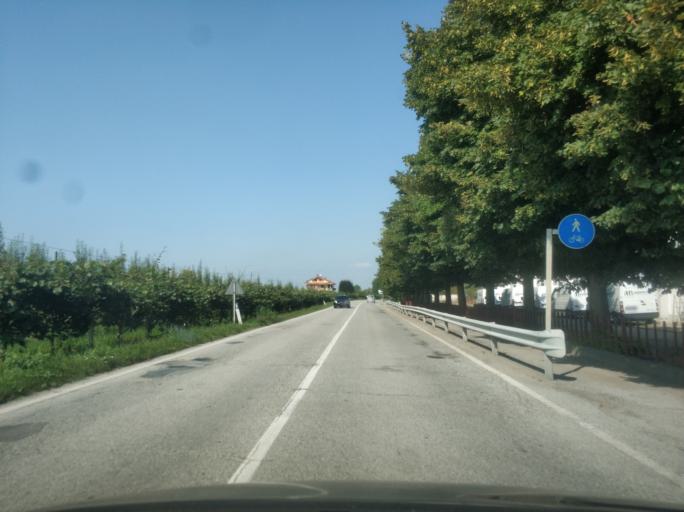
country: IT
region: Piedmont
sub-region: Provincia di Cuneo
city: Centallo
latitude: 44.5089
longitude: 7.5897
